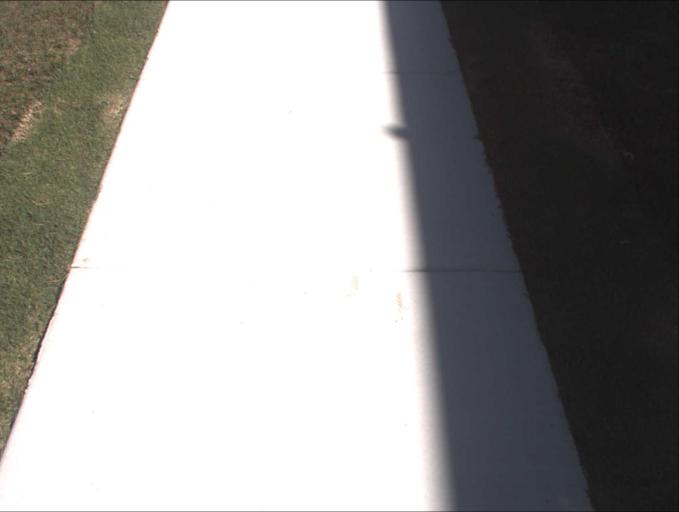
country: AU
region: Queensland
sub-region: Logan
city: Windaroo
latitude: -27.7272
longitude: 153.1844
